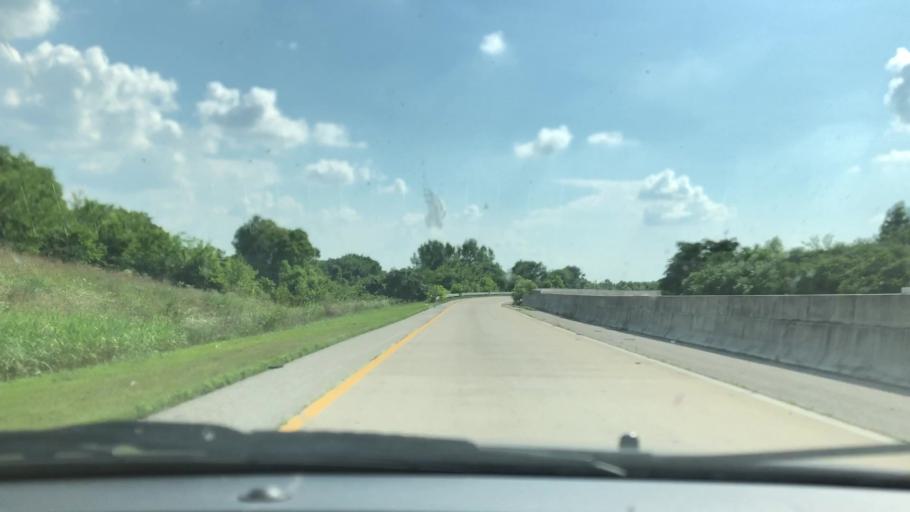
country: US
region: Tennessee
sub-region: Williamson County
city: Thompson's Station
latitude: 35.8200
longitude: -86.8378
